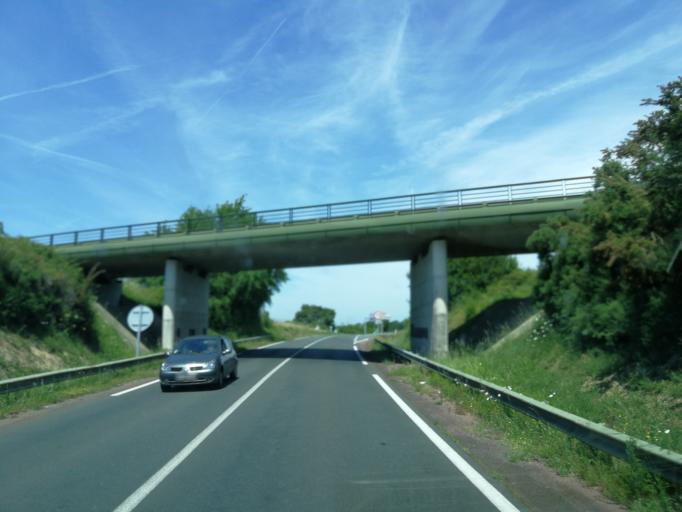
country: FR
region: Pays de la Loire
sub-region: Departement de la Vendee
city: Pissotte
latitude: 46.5481
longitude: -0.8064
